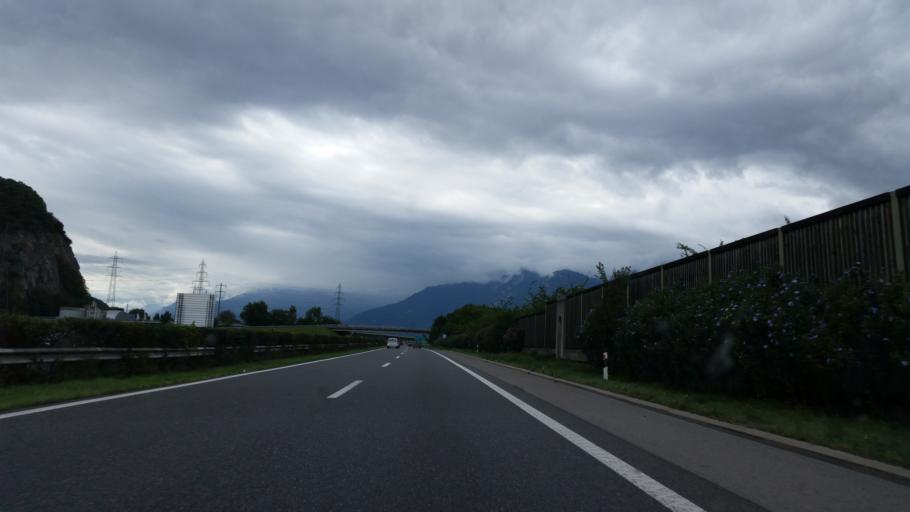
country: CH
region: Vaud
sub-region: Aigle District
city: Villeneuve
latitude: 46.3757
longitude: 6.9222
